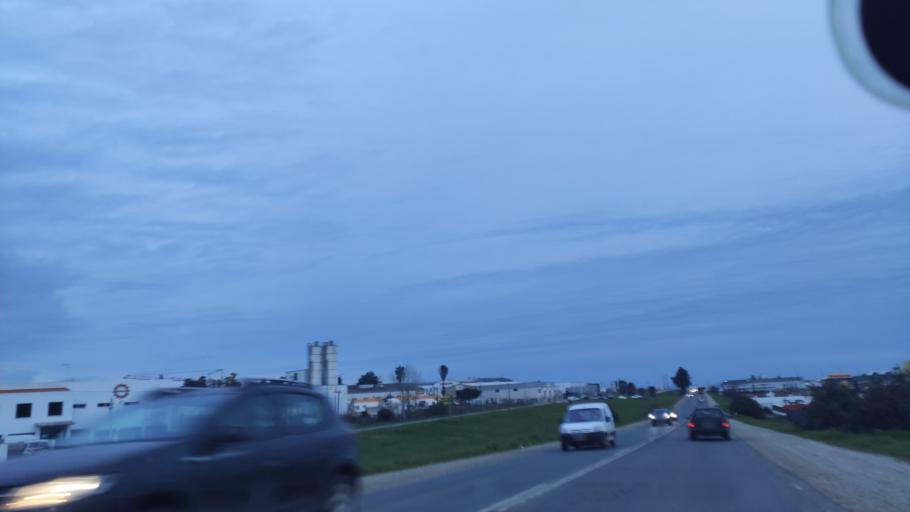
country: PT
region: Beja
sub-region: Beja
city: Beja
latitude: 38.0231
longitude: -7.8553
